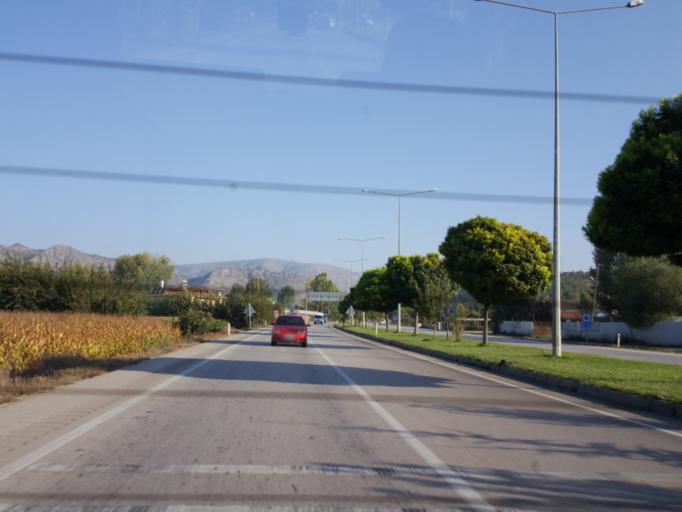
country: TR
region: Amasya
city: Amasya
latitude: 40.5709
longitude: 35.7869
